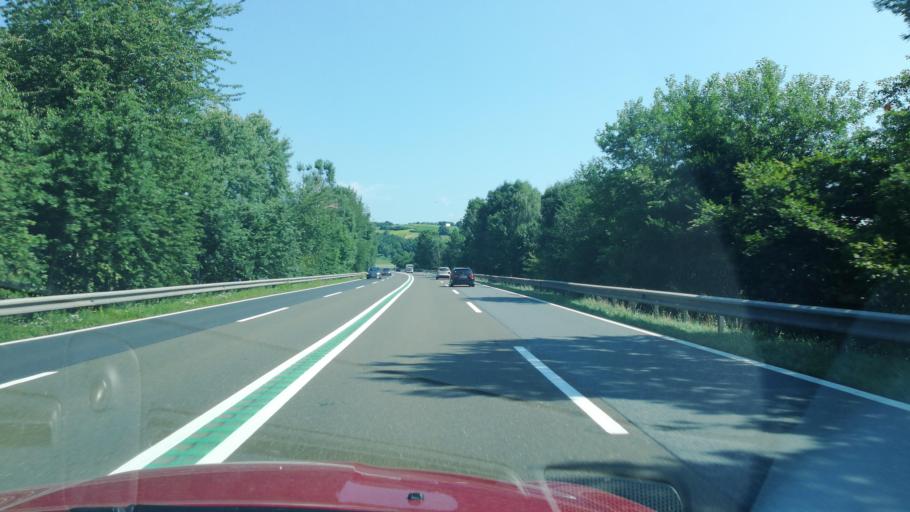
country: AT
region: Carinthia
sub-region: Politischer Bezirk Sankt Veit an der Glan
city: Sankt Veit an der Glan
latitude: 46.7350
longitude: 14.3843
